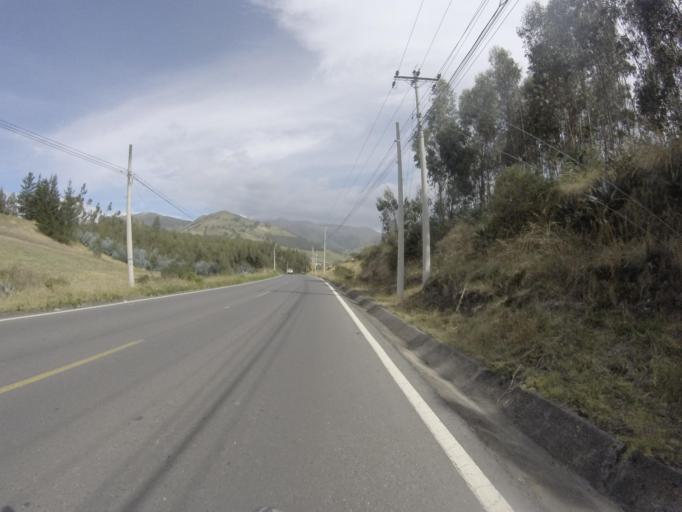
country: EC
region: Pichincha
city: Cayambe
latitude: 0.1274
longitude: -78.0808
